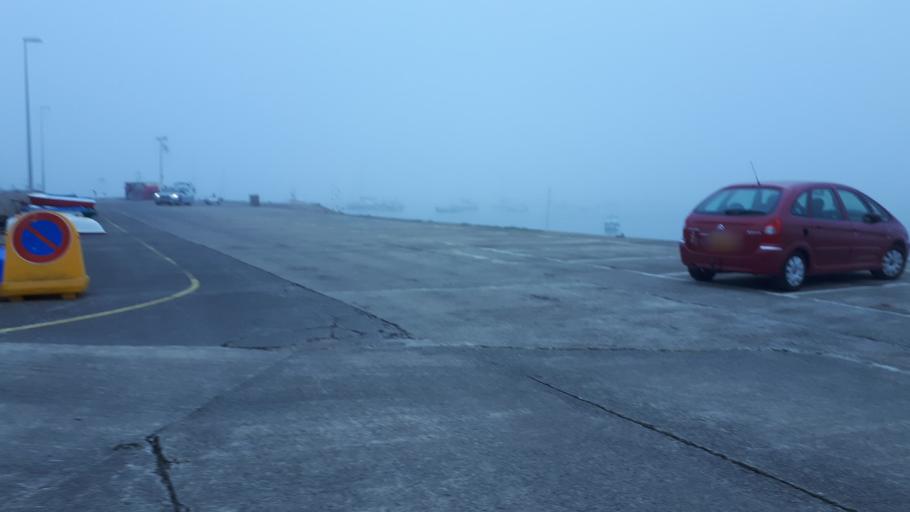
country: FR
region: Brittany
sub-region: Departement du Finistere
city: Plougasnou
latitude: 48.7118
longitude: -3.8277
